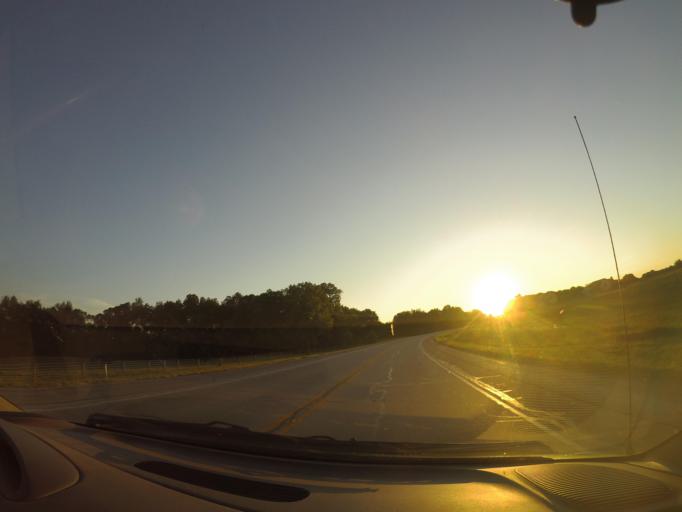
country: US
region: Indiana
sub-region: LaGrange County
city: Topeka
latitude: 41.6403
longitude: -85.5450
